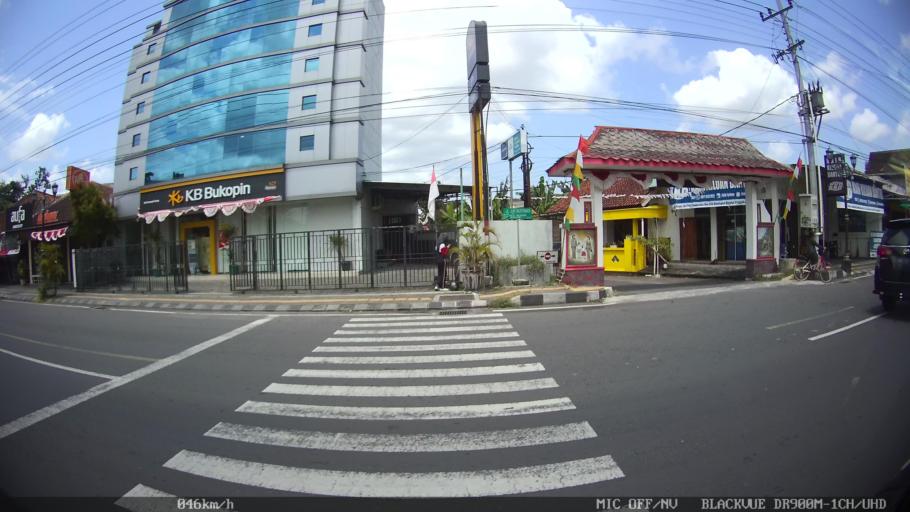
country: ID
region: Daerah Istimewa Yogyakarta
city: Bantul
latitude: -7.8876
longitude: 110.3289
